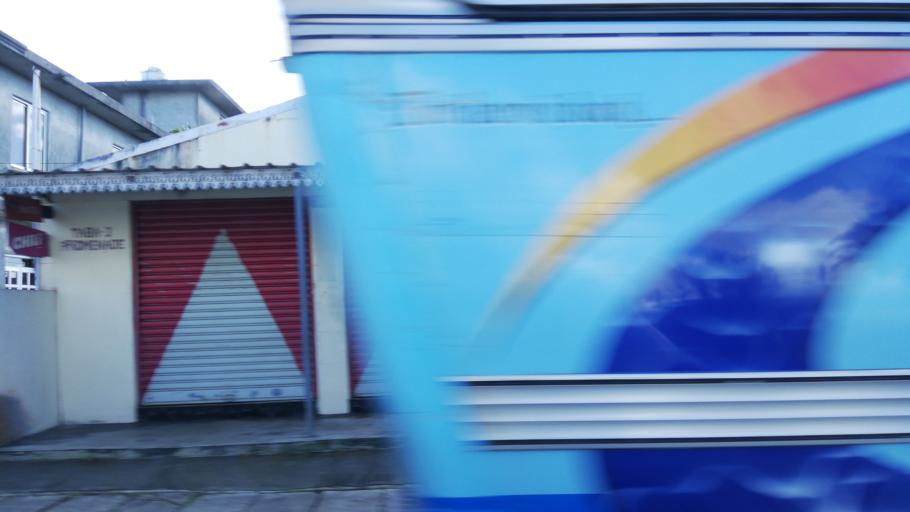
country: MU
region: Moka
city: Quartier Militaire
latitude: -20.2267
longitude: 57.5926
